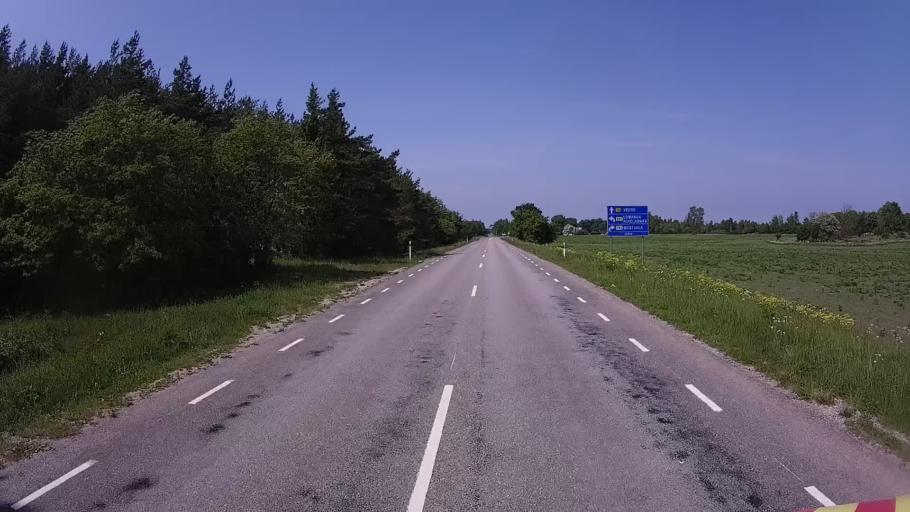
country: EE
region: Saare
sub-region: Kuressaare linn
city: Kuressaare
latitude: 58.3615
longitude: 22.0601
